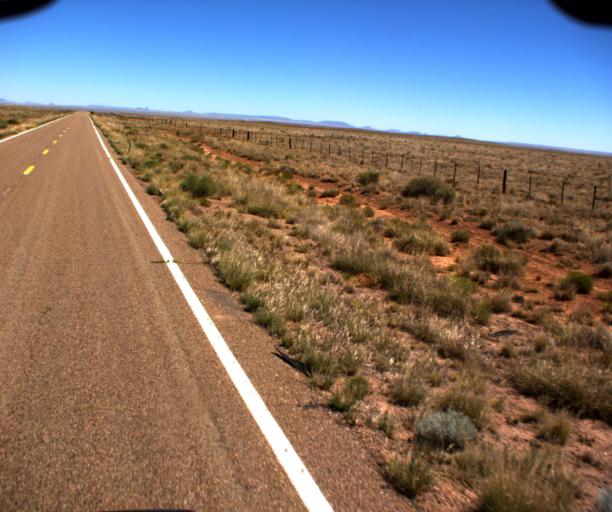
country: US
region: Arizona
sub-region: Navajo County
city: Winslow
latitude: 34.8865
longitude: -110.6496
